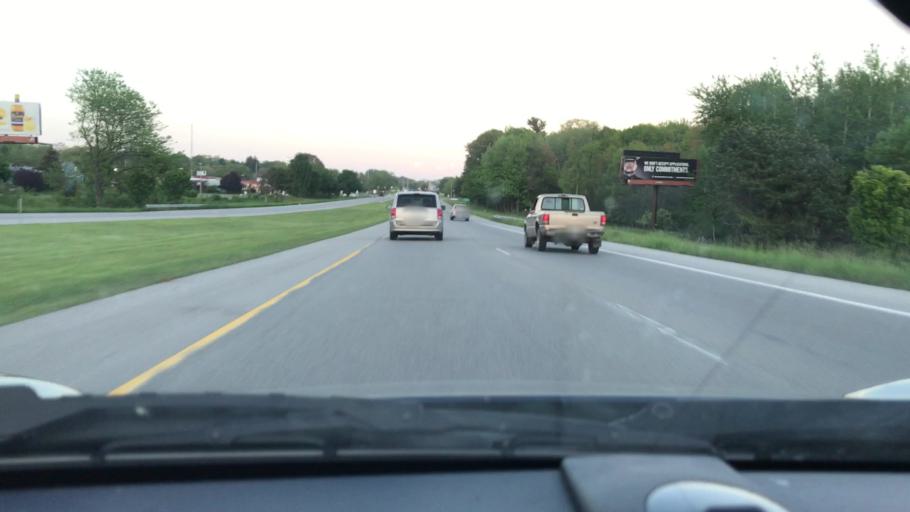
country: US
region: Michigan
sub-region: Muskegon County
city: Muskegon Heights
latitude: 43.1893
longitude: -86.2469
